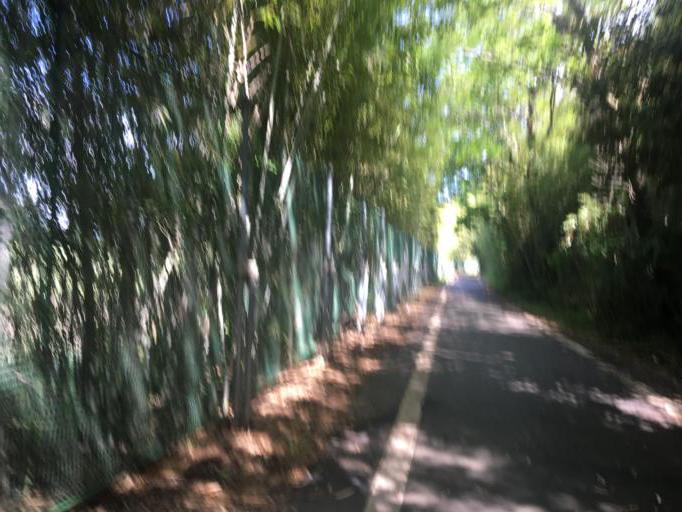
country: JP
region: Saitama
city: Shiki
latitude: 35.8639
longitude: 139.5848
